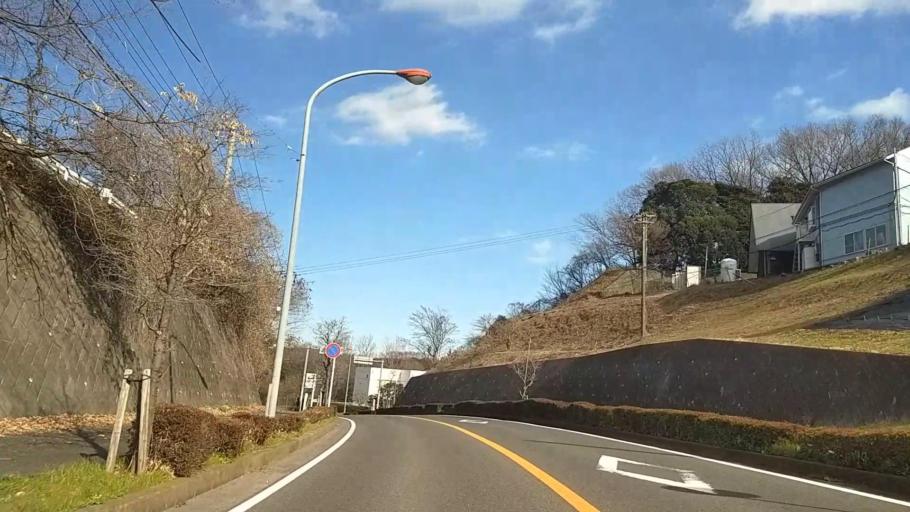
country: JP
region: Kanagawa
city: Isehara
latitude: 35.4274
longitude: 139.3044
